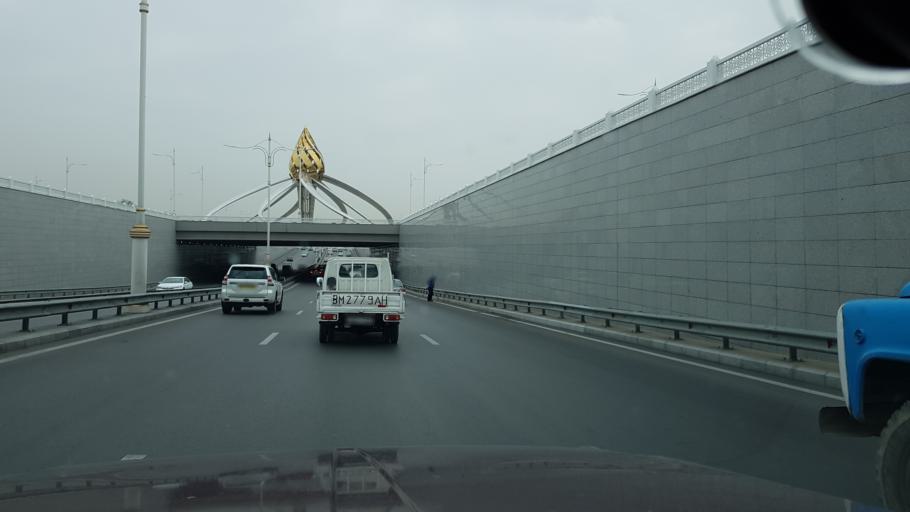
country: TM
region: Ahal
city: Ashgabat
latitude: 37.9206
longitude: 58.3891
